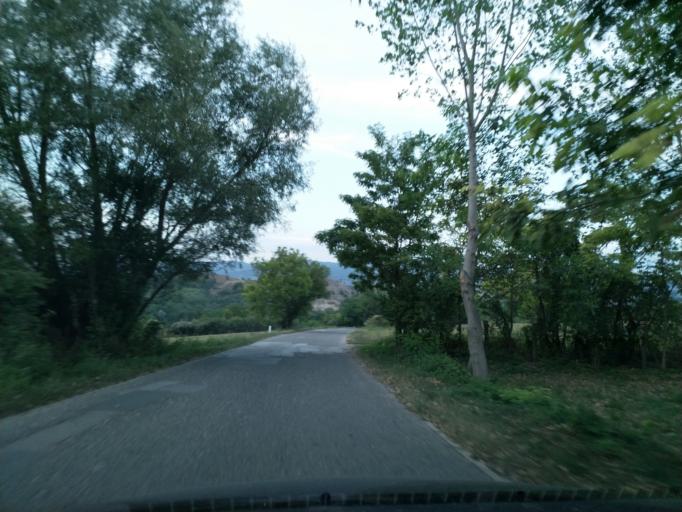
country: RS
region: Central Serbia
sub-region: Pomoravski Okrug
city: Paracin
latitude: 43.8545
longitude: 21.5288
